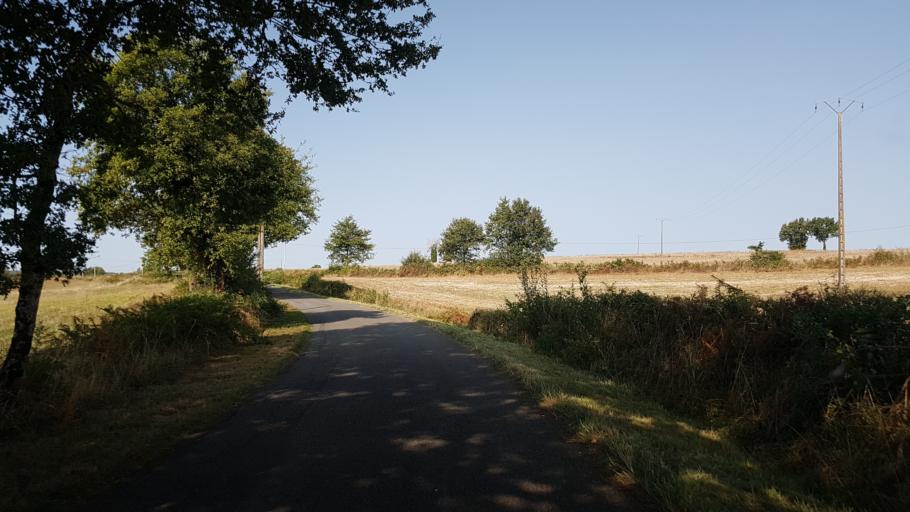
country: FR
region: Poitou-Charentes
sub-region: Departement de la Charente
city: Etagnac
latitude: 45.9253
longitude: 0.7662
